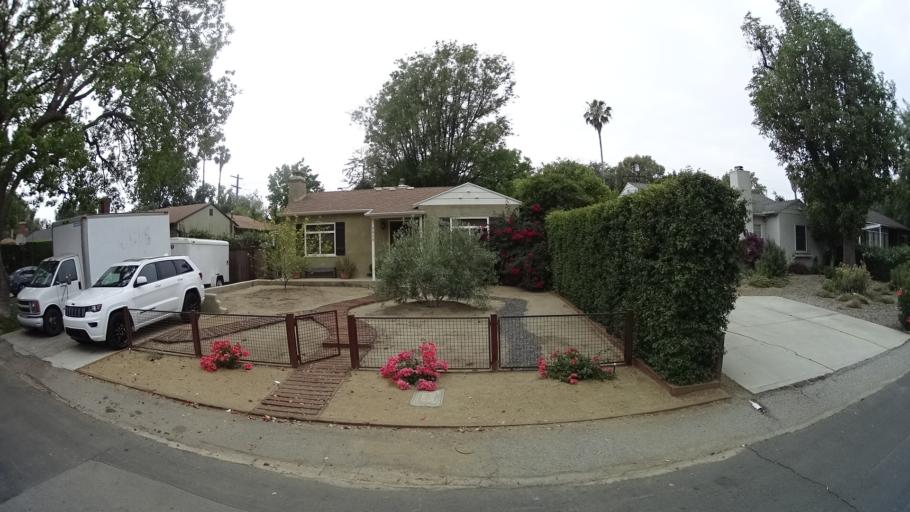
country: US
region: California
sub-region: Los Angeles County
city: Van Nuys
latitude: 34.1768
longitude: -118.4511
